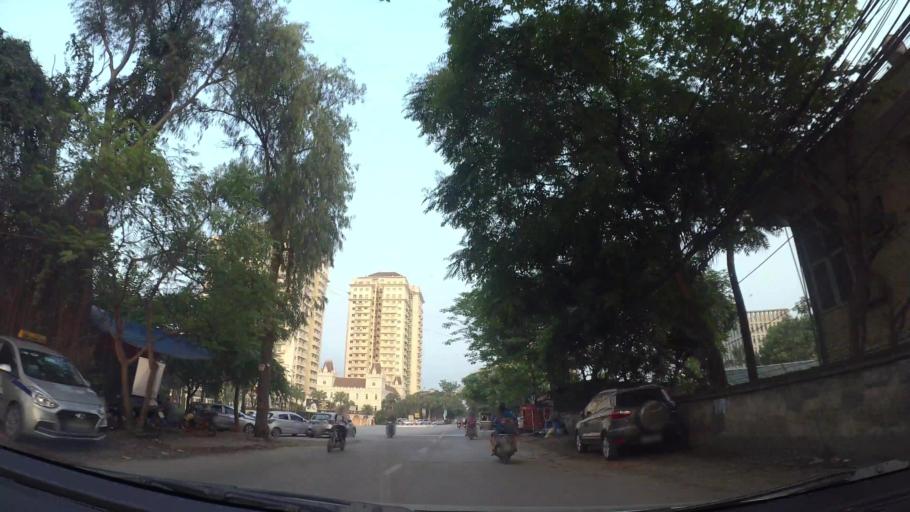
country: VN
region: Ha Noi
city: Tay Ho
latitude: 21.0741
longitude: 105.7994
